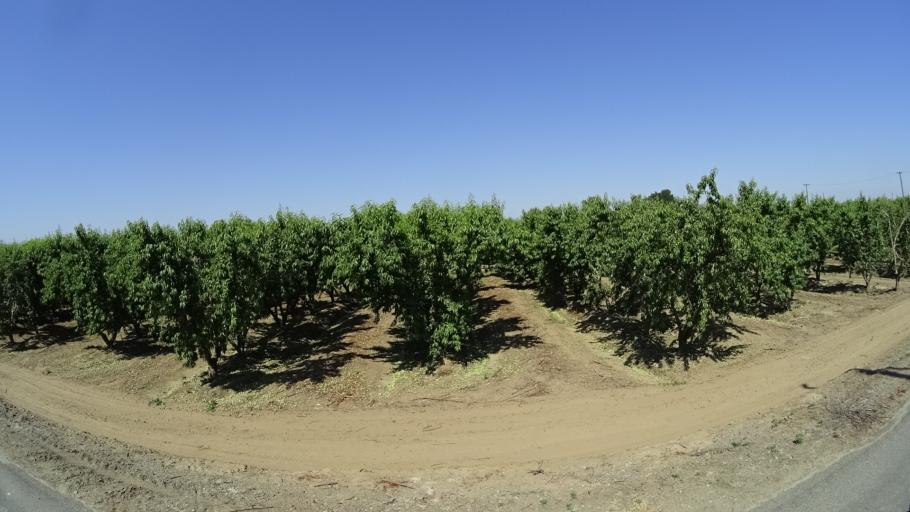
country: US
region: California
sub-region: Fresno County
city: Kingsburg
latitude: 36.4481
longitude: -119.5630
